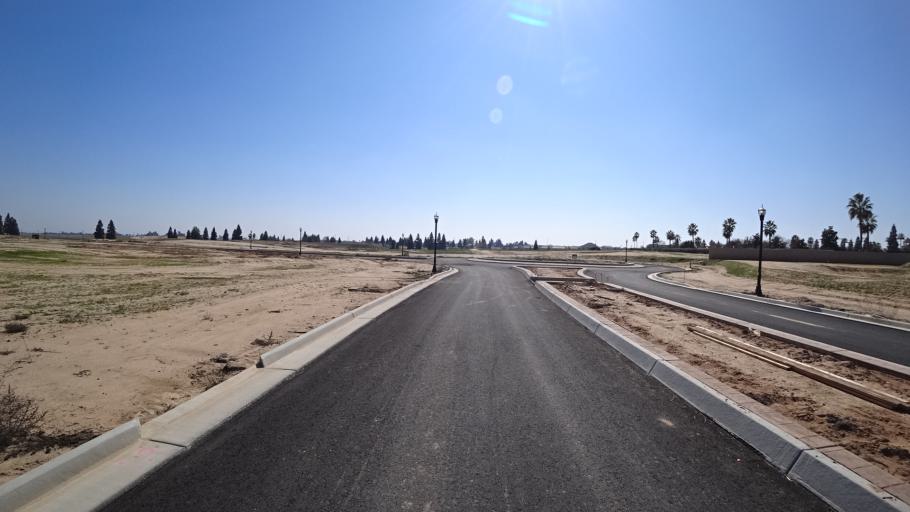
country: US
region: California
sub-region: Fresno County
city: Clovis
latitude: 36.9046
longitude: -119.7394
